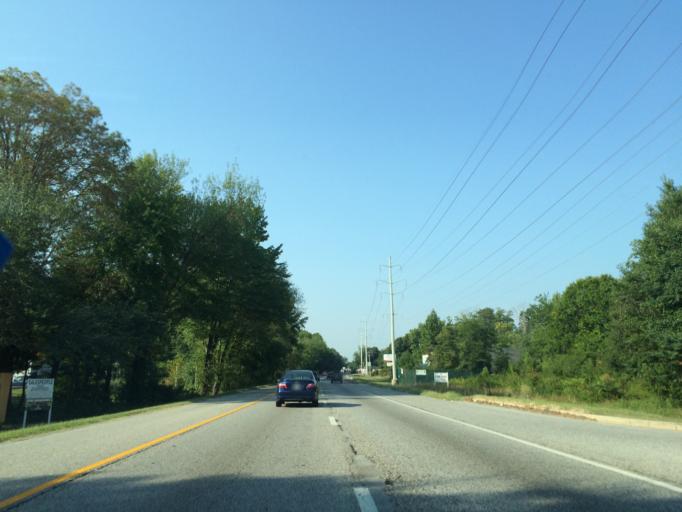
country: US
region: Maryland
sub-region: Anne Arundel County
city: Gambrills
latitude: 39.0489
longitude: -76.6641
